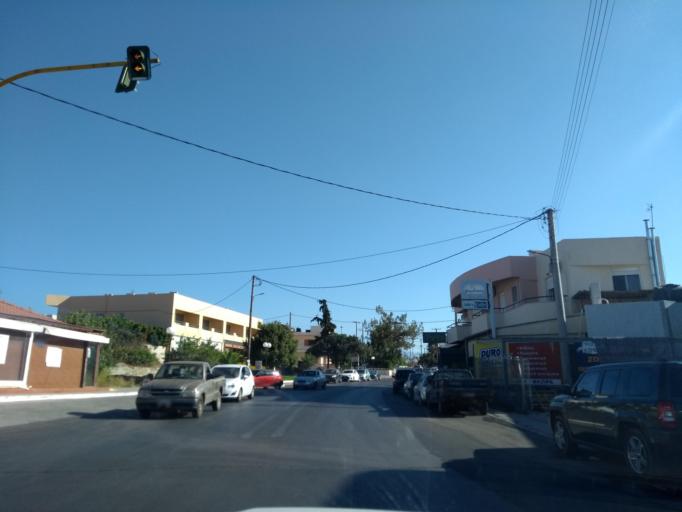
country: GR
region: Crete
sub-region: Nomos Chanias
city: Pithari
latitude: 35.5320
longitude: 24.0762
